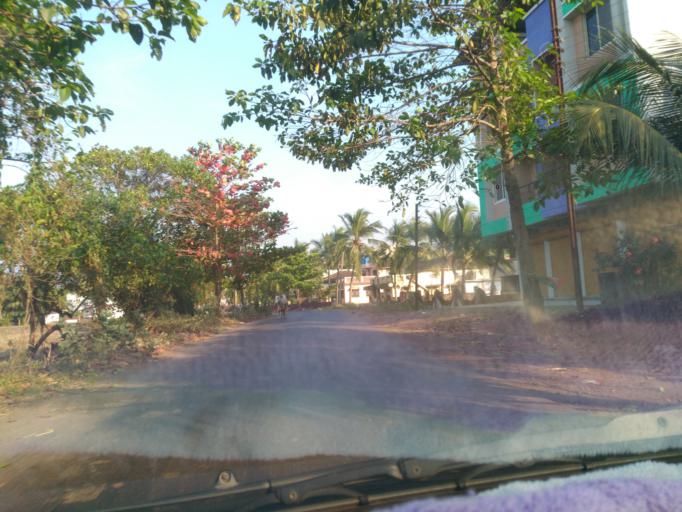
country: IN
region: Maharashtra
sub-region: Raigarh
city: Mhasla
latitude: 18.1672
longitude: 72.9994
